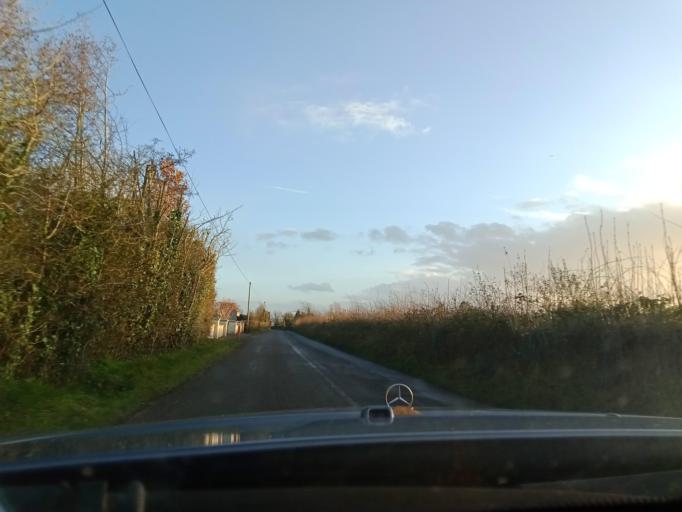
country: IE
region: Leinster
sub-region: Kilkenny
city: Callan
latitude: 52.5016
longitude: -7.3422
